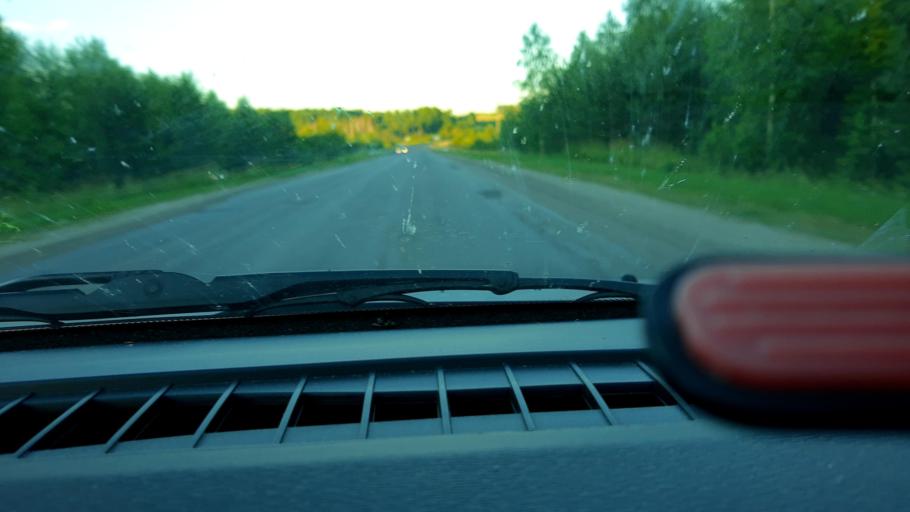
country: RU
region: Nizjnij Novgorod
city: Uren'
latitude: 57.5036
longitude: 45.8592
